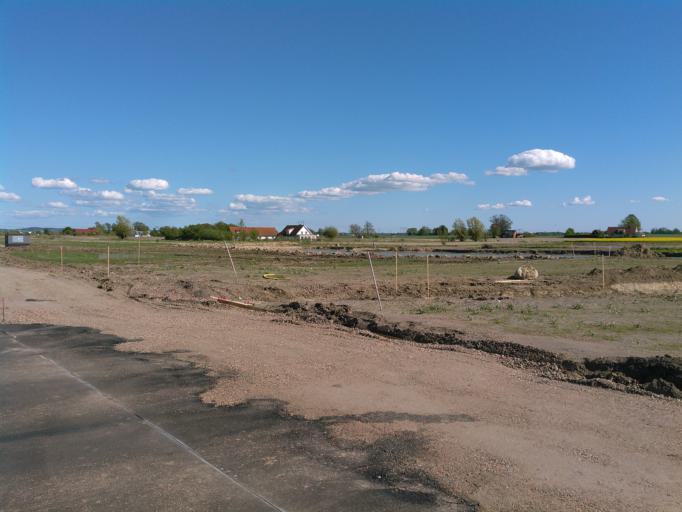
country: SE
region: Skane
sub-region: Lunds Kommun
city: Lund
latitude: 55.6903
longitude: 13.2281
